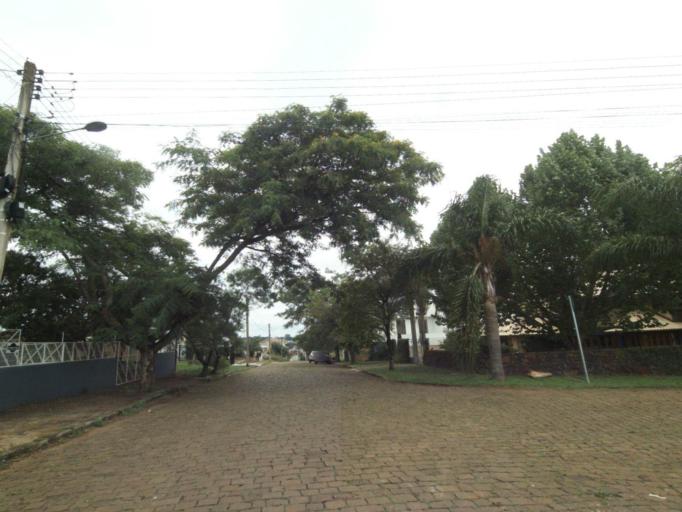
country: BR
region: Rio Grande do Sul
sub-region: Lagoa Vermelha
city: Lagoa Vermelha
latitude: -28.2165
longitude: -51.5326
